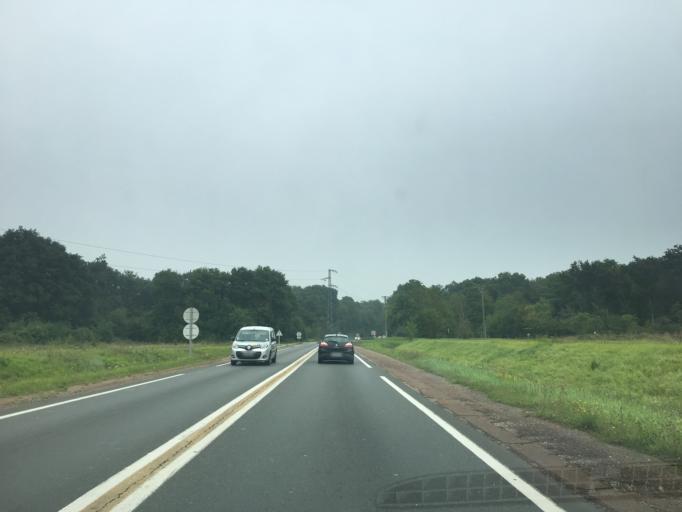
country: FR
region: Ile-de-France
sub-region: Departement de l'Essonne
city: Tigery
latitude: 48.6563
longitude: 2.5114
